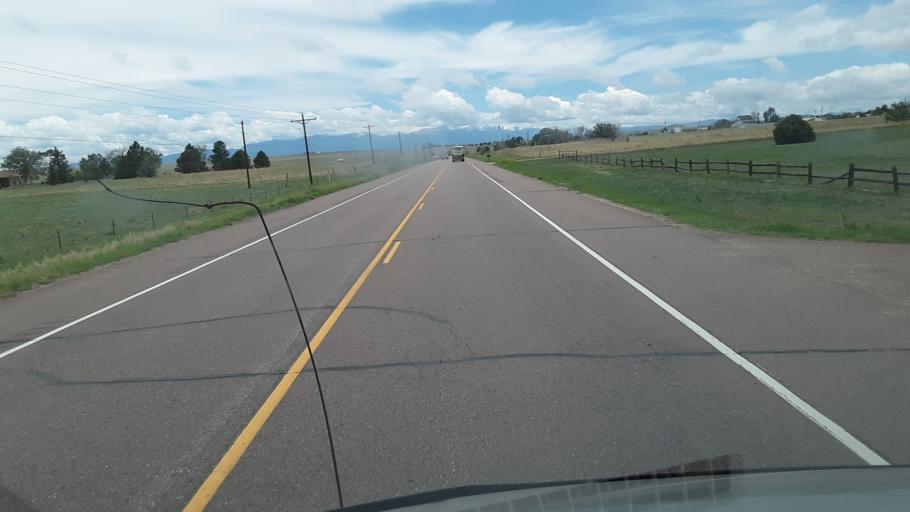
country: US
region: Colorado
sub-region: El Paso County
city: Ellicott
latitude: 38.8386
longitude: -104.5104
